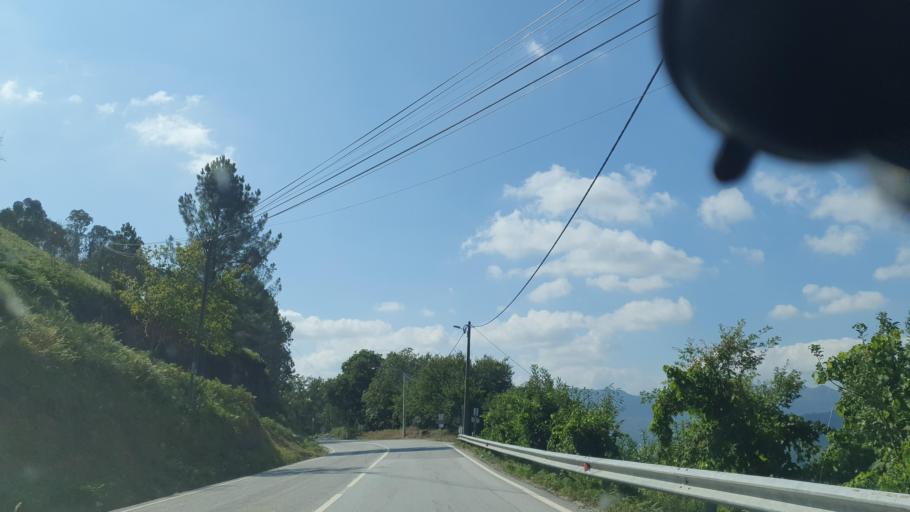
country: PT
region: Braga
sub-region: Vieira do Minho
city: Vieira do Minho
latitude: 41.6719
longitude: -8.1511
